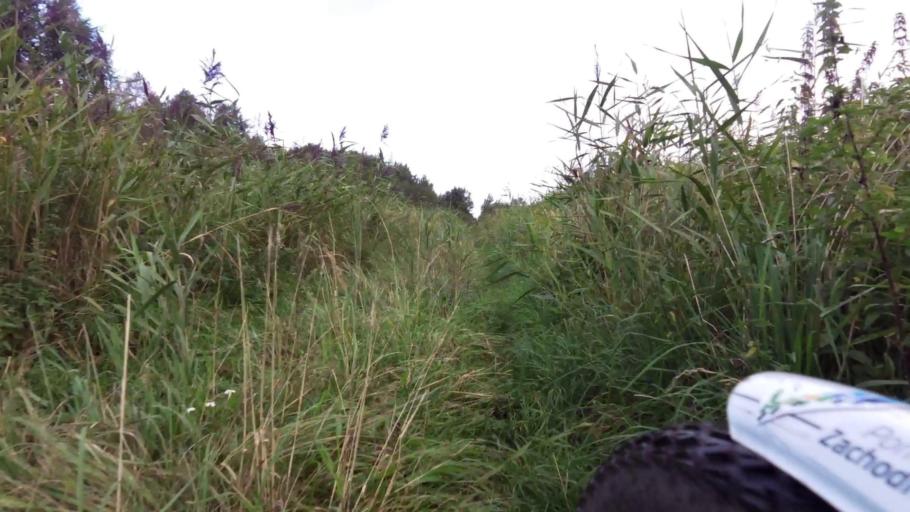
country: PL
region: West Pomeranian Voivodeship
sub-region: Powiat kolobrzeski
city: Grzybowo
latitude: 54.1487
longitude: 15.4586
